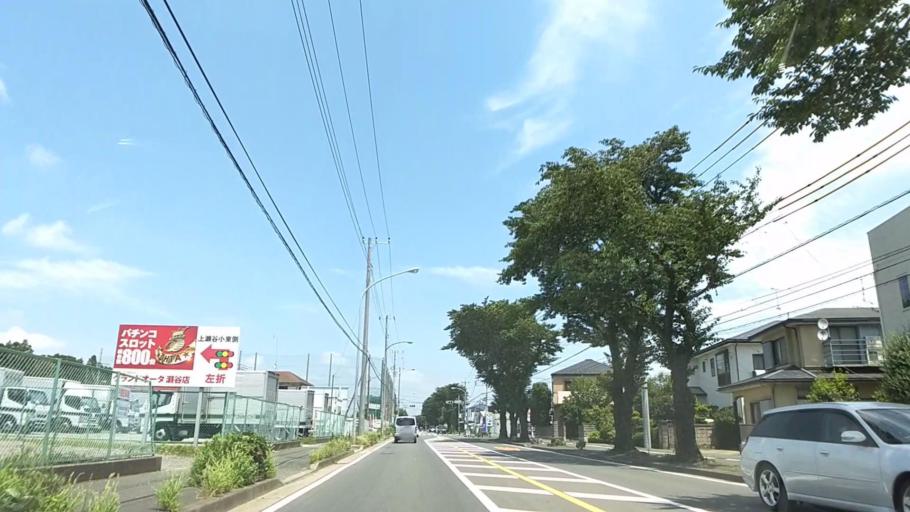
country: JP
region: Kanagawa
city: Minami-rinkan
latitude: 35.4799
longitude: 139.4805
